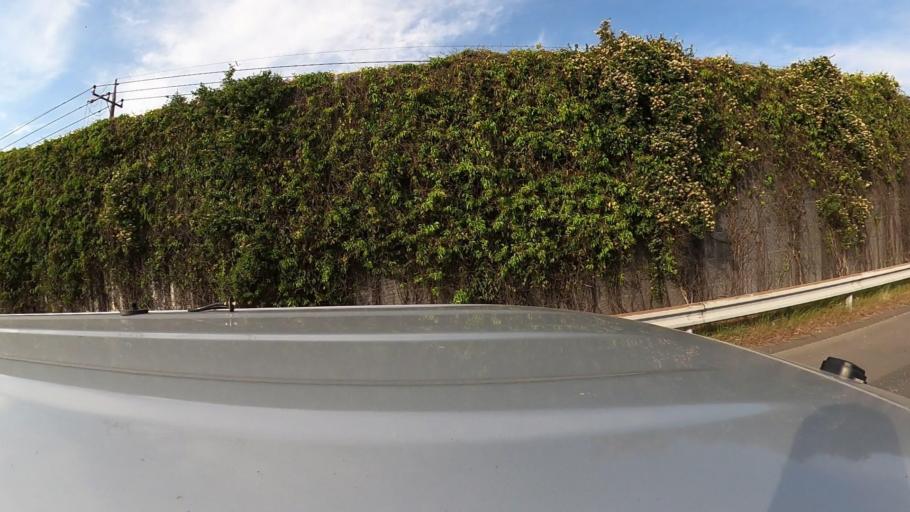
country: JP
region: Saitama
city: Kamifukuoka
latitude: 35.8614
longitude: 139.4904
